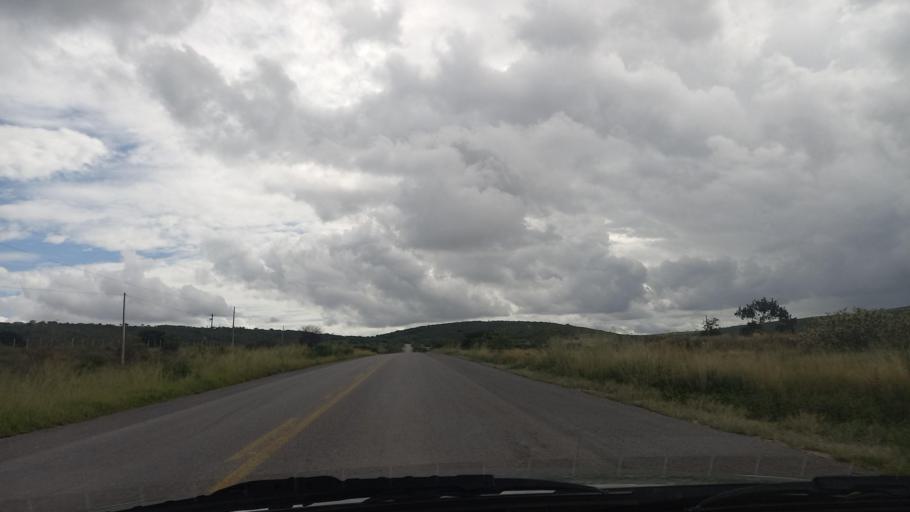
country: BR
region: Pernambuco
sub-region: Lajedo
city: Lajedo
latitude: -8.6710
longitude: -36.3865
